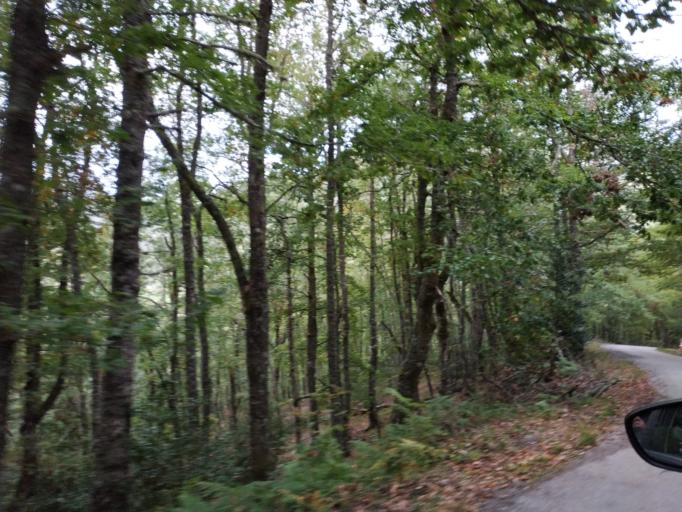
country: ES
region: Castille and Leon
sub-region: Provincia de Leon
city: Candin
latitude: 42.8649
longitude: -6.8631
